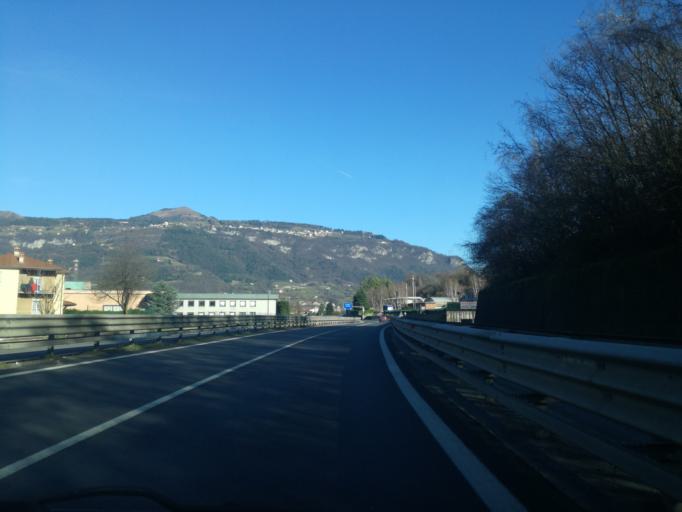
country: IT
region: Lombardy
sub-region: Provincia di Bergamo
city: Sovere
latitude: 45.8037
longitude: 10.0219
